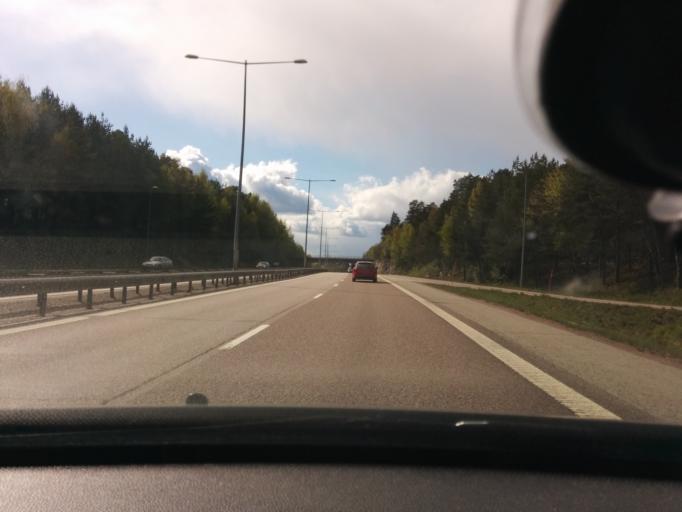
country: SE
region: Vaestmanland
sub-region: Vasteras
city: Vasteras
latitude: 59.6095
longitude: 16.5977
